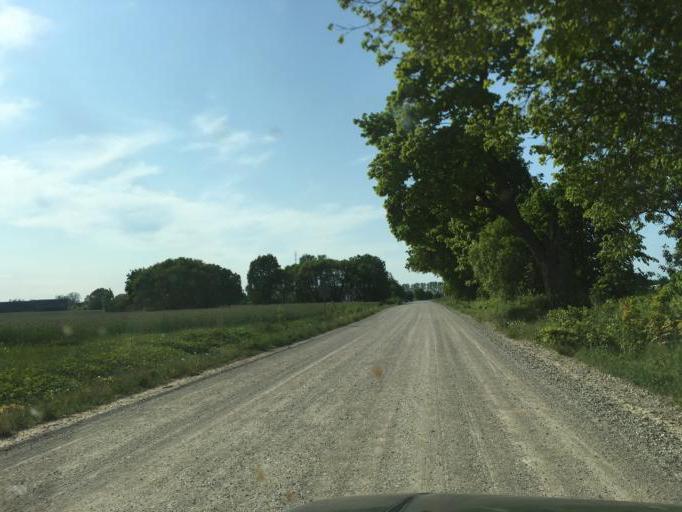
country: LV
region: Dundaga
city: Dundaga
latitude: 57.6070
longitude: 22.4634
